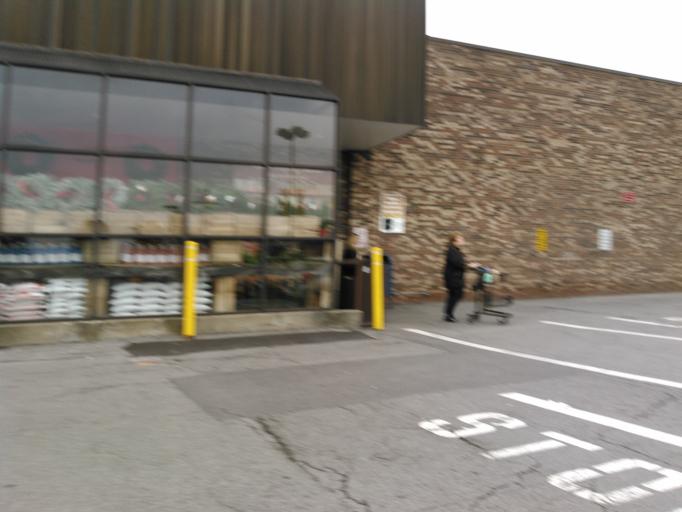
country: US
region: New York
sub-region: Onondaga County
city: East Syracuse
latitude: 43.0685
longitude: -76.0872
